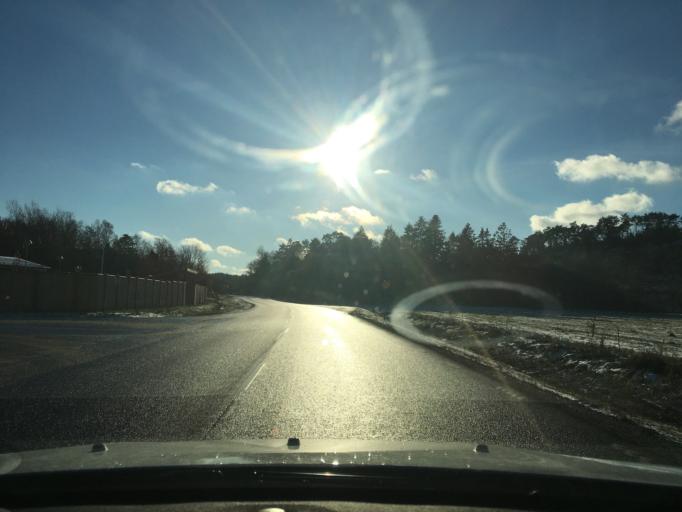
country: SE
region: Vaestra Goetaland
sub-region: Tjorns Kommun
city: Myggenas
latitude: 58.0293
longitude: 11.6563
